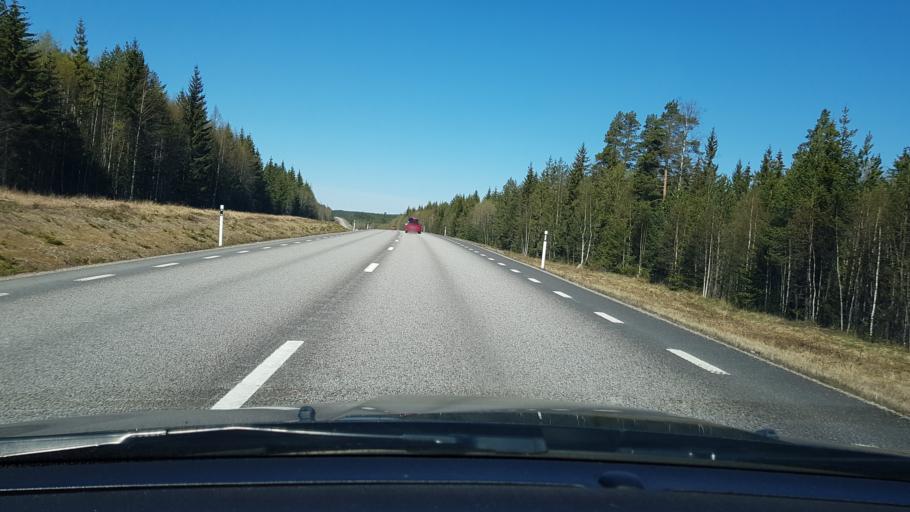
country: SE
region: Dalarna
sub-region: Rattviks Kommun
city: Raettvik
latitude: 60.8385
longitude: 15.2172
